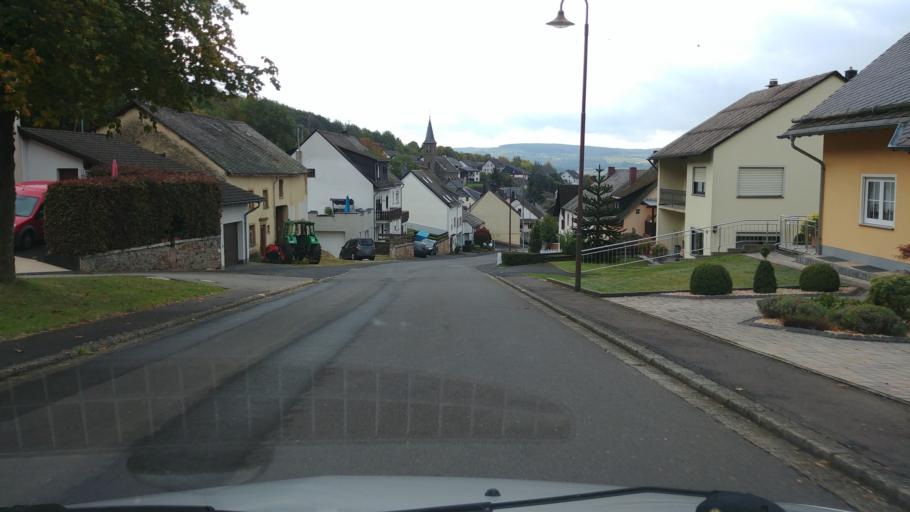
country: DE
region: Rheinland-Pfalz
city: Horath
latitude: 49.8138
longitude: 6.9866
